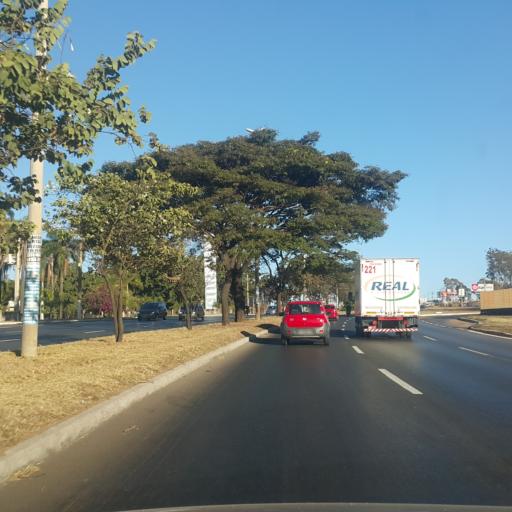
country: BR
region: Federal District
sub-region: Brasilia
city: Brasilia
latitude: -15.8364
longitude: -48.0671
